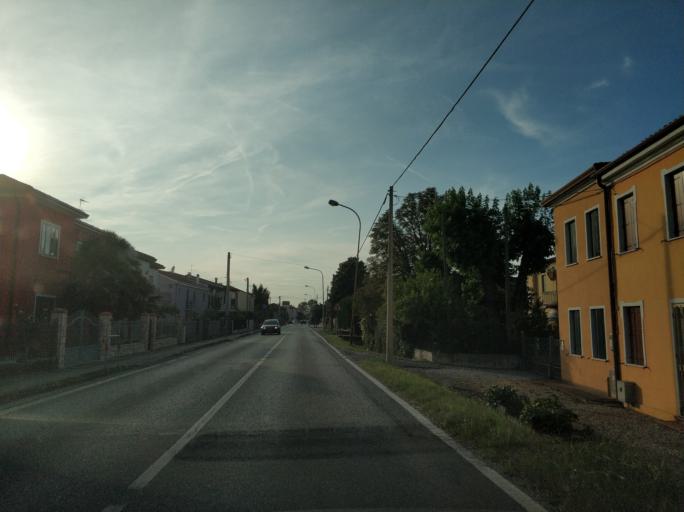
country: IT
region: Veneto
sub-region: Provincia di Padova
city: Este
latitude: 45.2176
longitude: 11.6666
